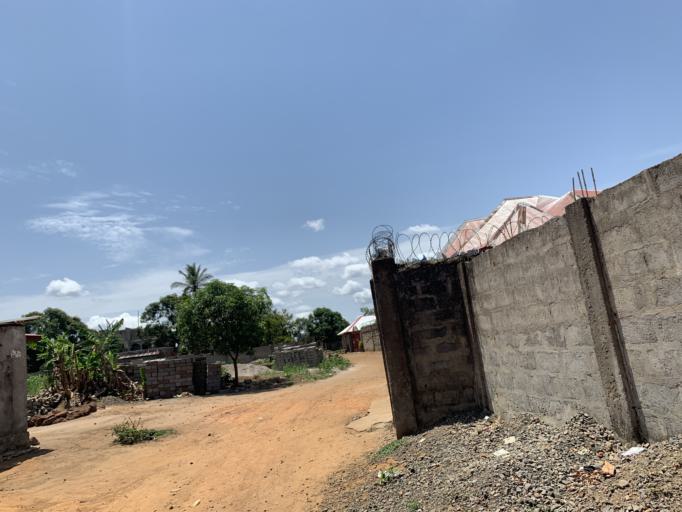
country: SL
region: Western Area
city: Waterloo
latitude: 8.3153
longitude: -13.0725
